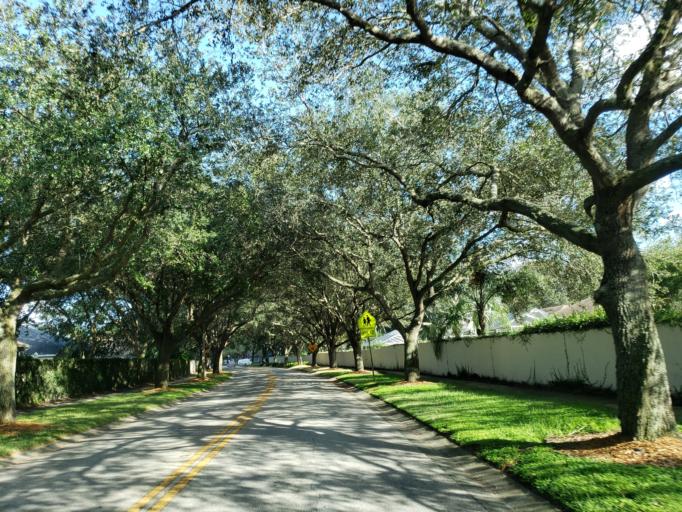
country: US
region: Florida
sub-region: Hillsborough County
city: Bloomingdale
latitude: 27.8737
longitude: -82.2461
